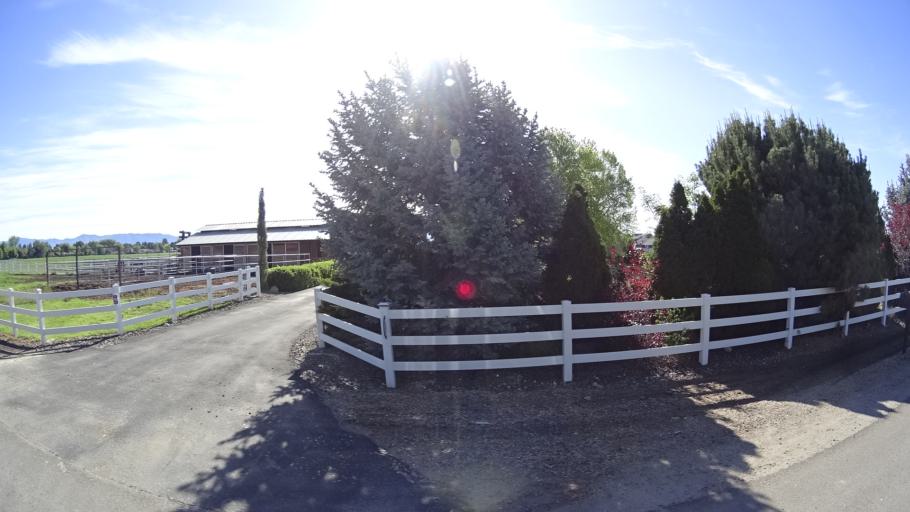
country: US
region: Idaho
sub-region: Ada County
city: Garden City
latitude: 43.5508
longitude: -116.2743
